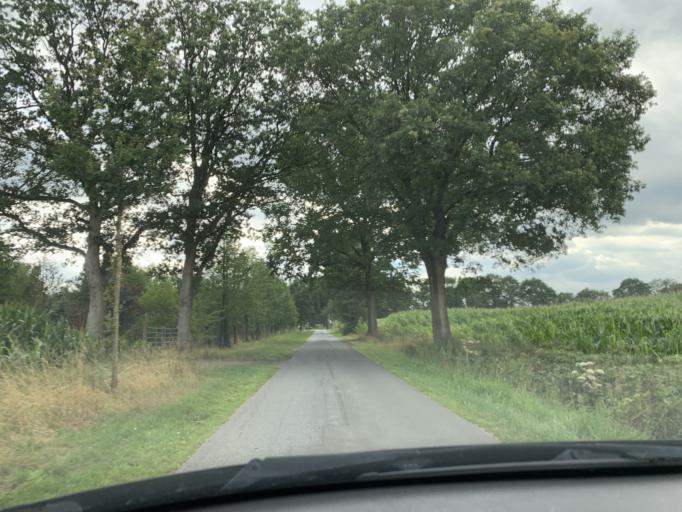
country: DE
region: Lower Saxony
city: Westerstede
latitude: 53.2440
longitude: 7.8669
